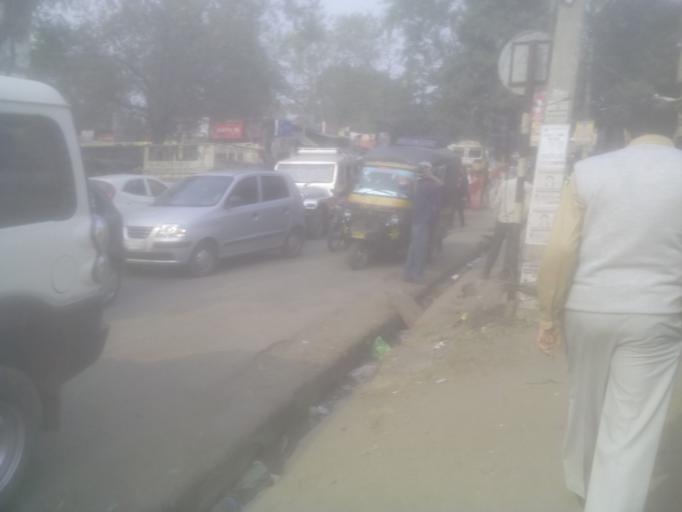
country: IN
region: Jharkhand
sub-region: Dhanbad
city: Dhanbad
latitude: 23.8068
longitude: 86.4318
